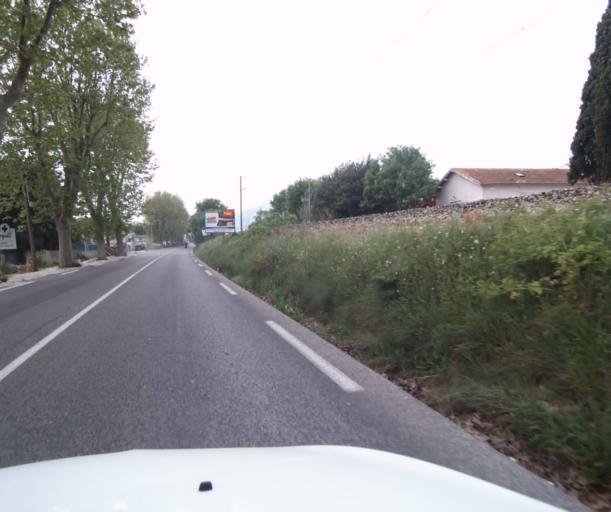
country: FR
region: Provence-Alpes-Cote d'Azur
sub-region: Departement du Var
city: La Valette-du-Var
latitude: 43.1149
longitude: 5.9860
